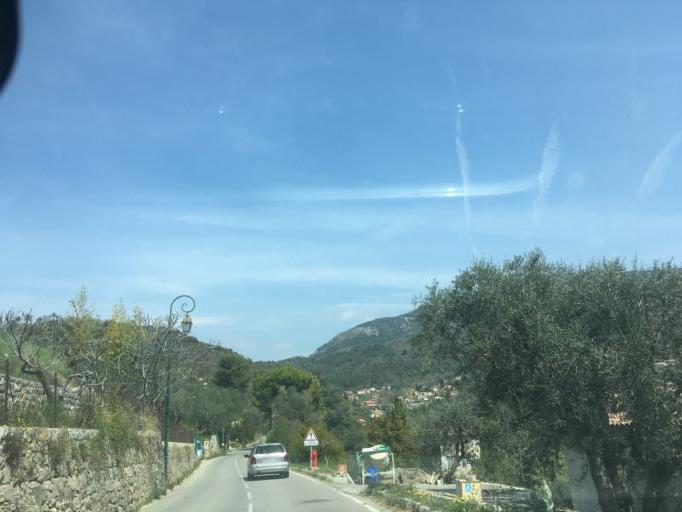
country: FR
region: Provence-Alpes-Cote d'Azur
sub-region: Departement des Alpes-Maritimes
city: Levens
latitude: 43.8485
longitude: 7.2226
